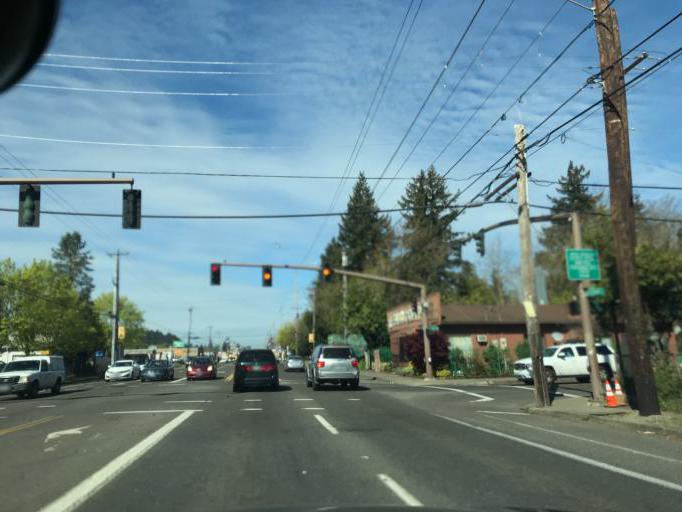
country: US
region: Oregon
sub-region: Multnomah County
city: Lents
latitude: 45.5040
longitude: -122.5294
